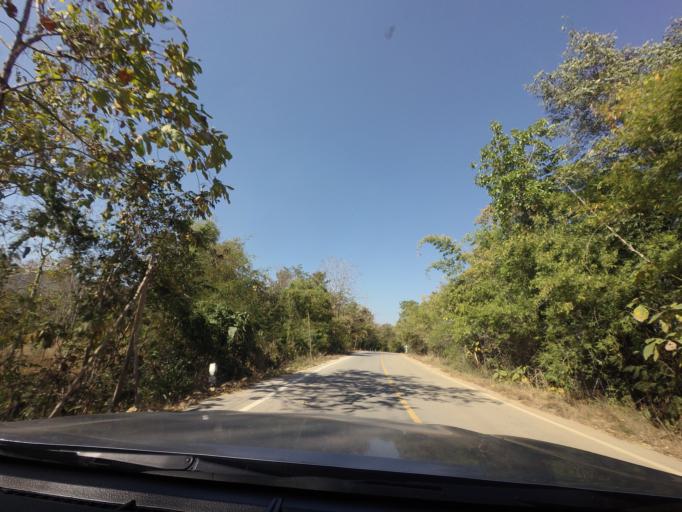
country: TH
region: Lampang
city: Chae Hom
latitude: 18.5323
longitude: 99.6425
